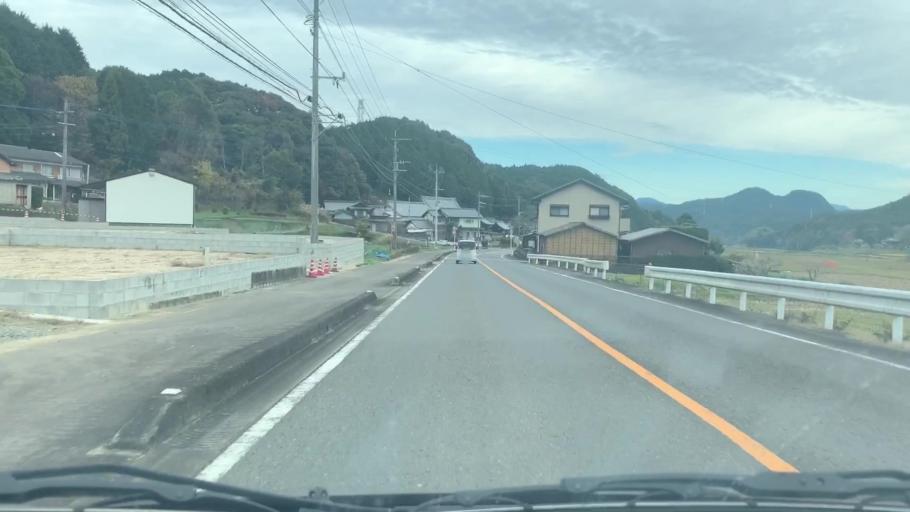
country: JP
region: Saga Prefecture
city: Takeocho-takeo
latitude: 33.1756
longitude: 129.9706
